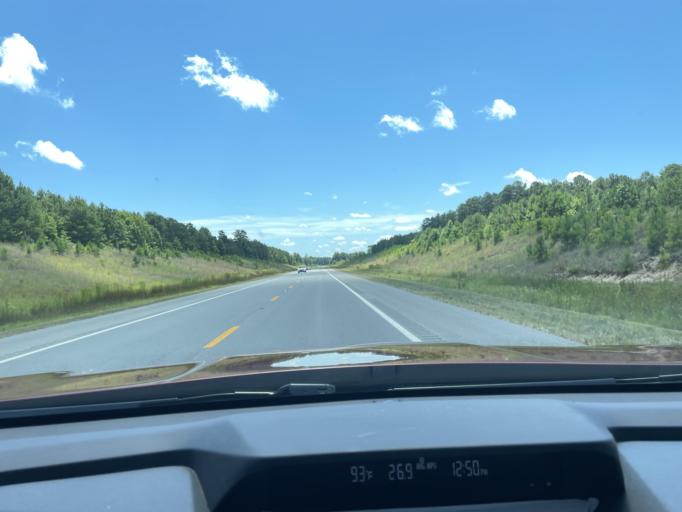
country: US
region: Arkansas
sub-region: Lincoln County
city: Star City
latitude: 33.9468
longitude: -91.8991
